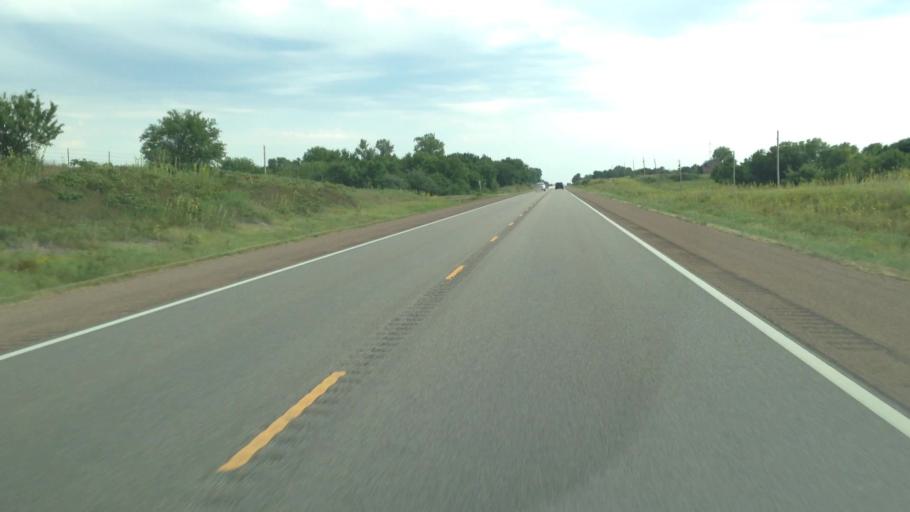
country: US
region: Kansas
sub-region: Woodson County
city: Yates Center
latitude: 37.9972
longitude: -95.7388
